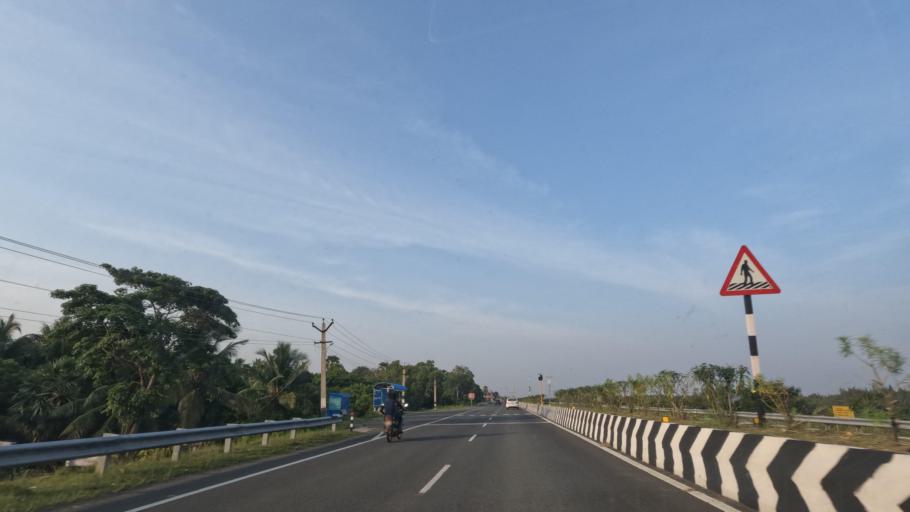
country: IN
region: Tamil Nadu
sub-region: Kancheepuram
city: Mamallapuram
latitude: 12.7138
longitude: 80.2263
